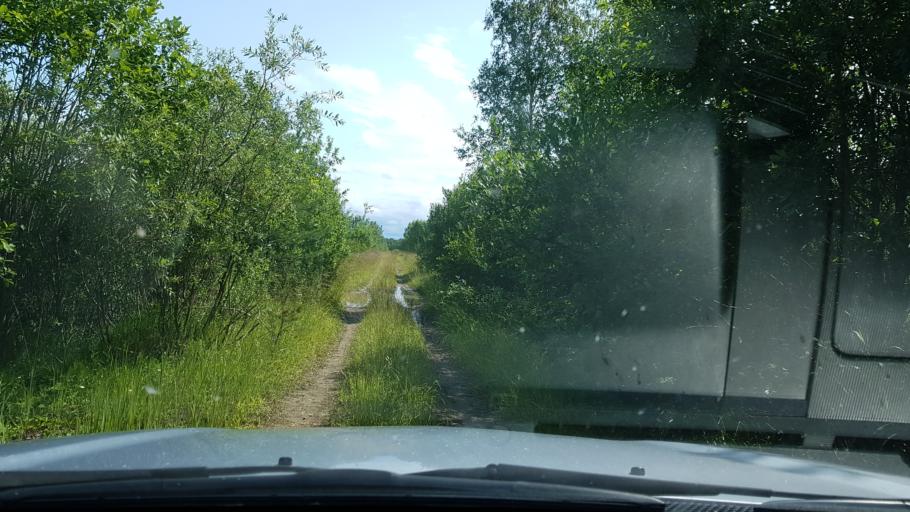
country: EE
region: Ida-Virumaa
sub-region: Sillamaee linn
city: Sillamae
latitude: 59.3662
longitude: 27.7966
